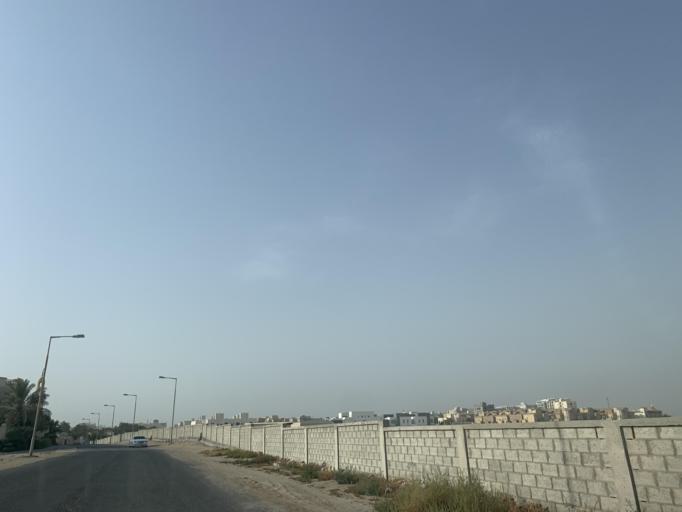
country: BH
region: Central Governorate
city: Madinat Hamad
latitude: 26.1751
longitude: 50.4765
